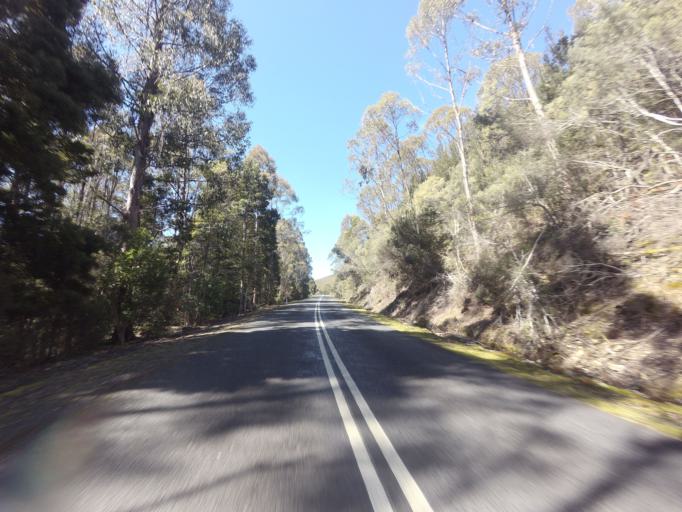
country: AU
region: Tasmania
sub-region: Derwent Valley
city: New Norfolk
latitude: -42.7219
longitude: 146.4379
